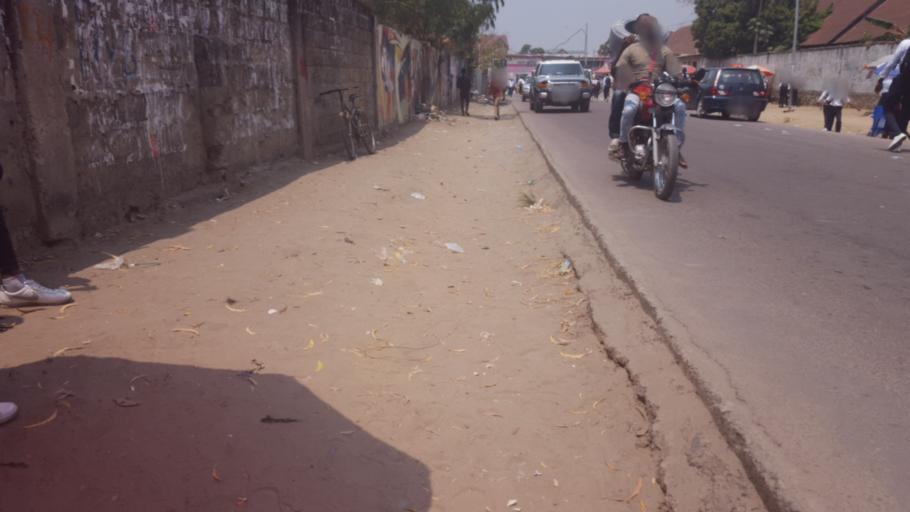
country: CD
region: Kinshasa
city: Kinshasa
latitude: -4.3224
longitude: 15.2937
